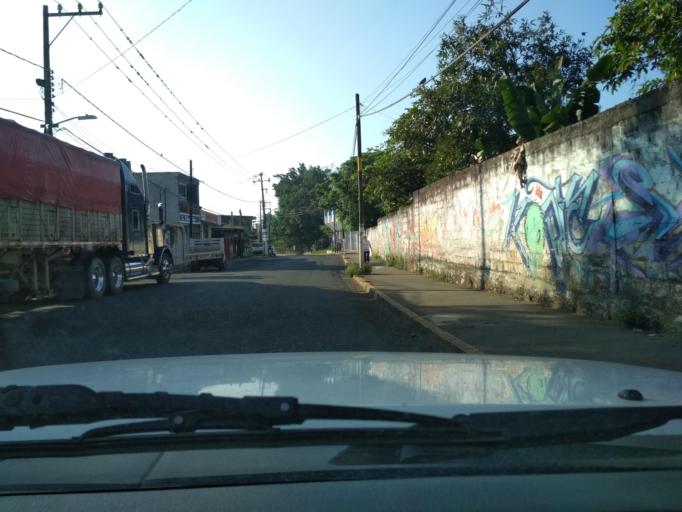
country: MX
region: Veracruz
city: Cordoba
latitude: 18.8728
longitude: -96.9330
